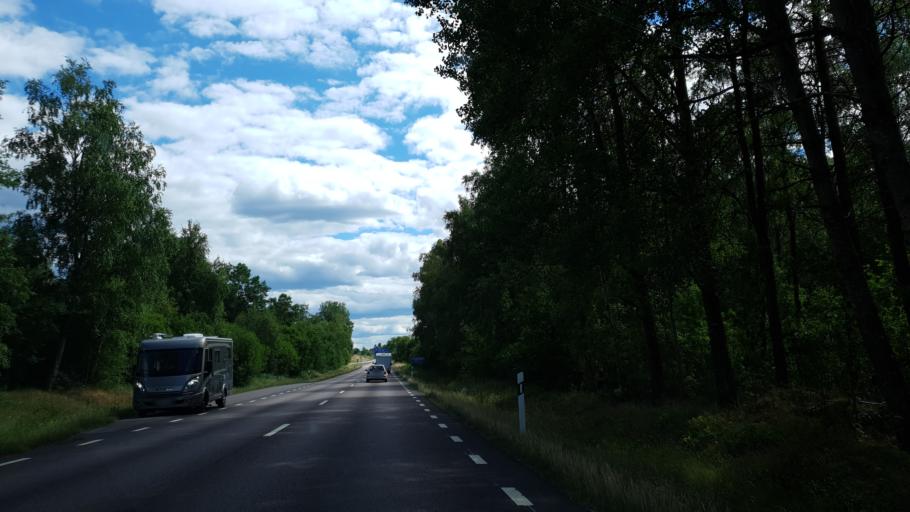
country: SE
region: Kronoberg
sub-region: Lessebo Kommun
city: Lessebo
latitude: 56.8535
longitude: 15.3884
